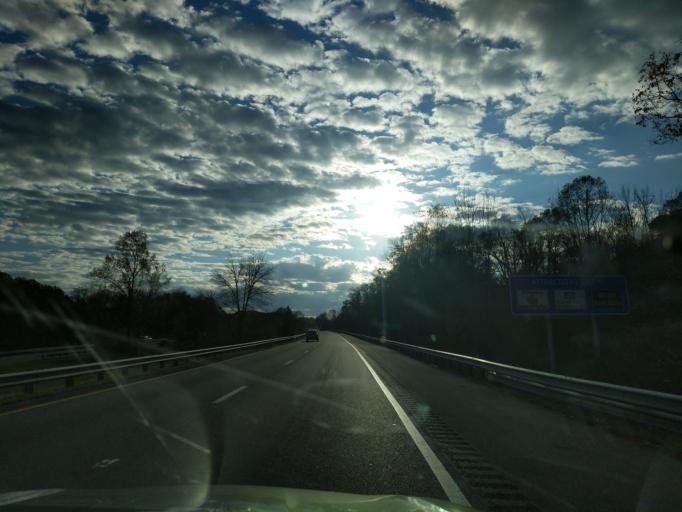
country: US
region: Virginia
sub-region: Washington County
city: Abingdon
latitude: 36.7072
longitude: -81.9511
